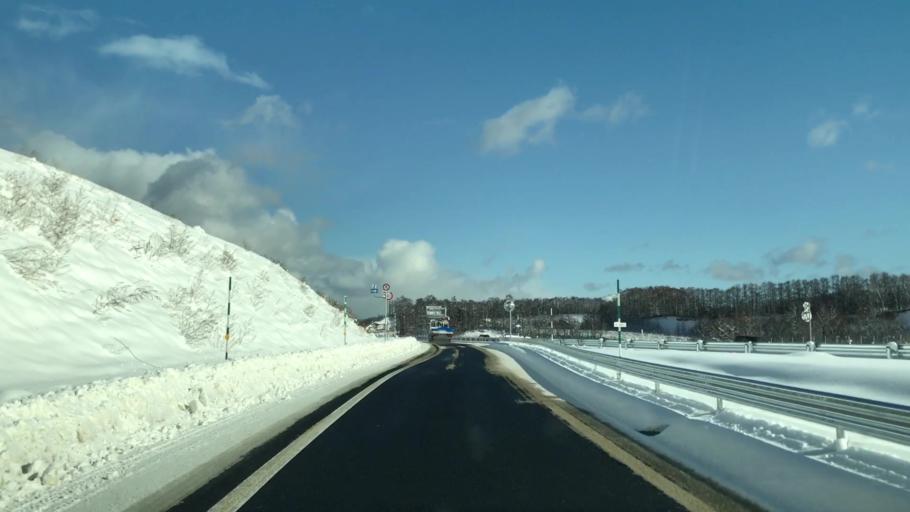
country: JP
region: Hokkaido
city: Yoichi
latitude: 43.1829
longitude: 140.8264
